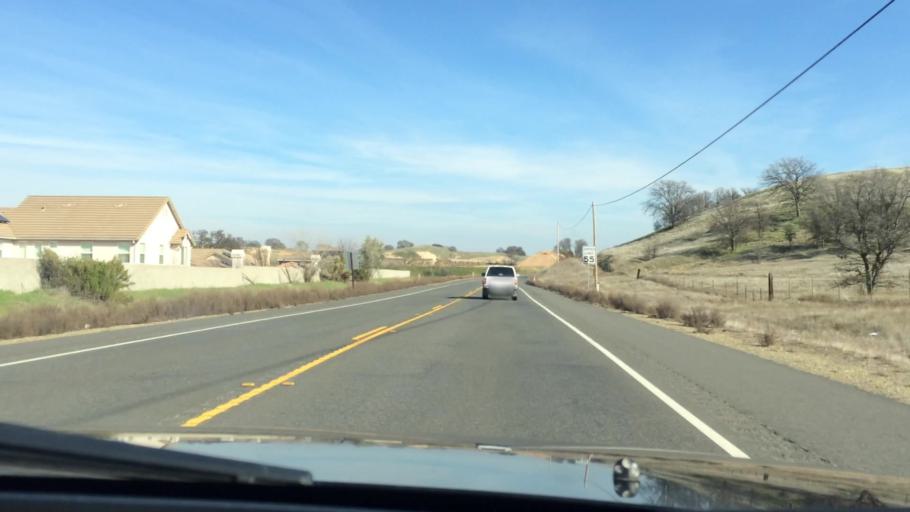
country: US
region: California
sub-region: Sacramento County
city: Rancho Murieta
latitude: 38.4854
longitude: -121.0665
